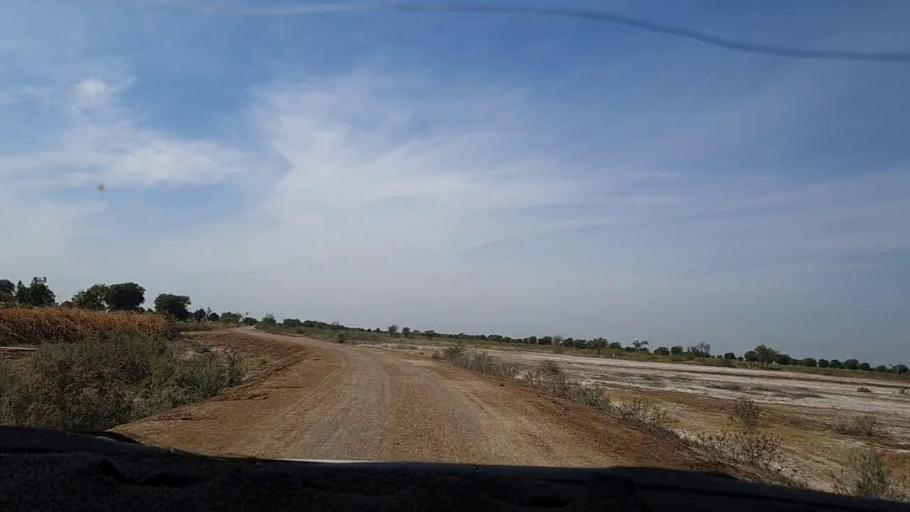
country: PK
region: Sindh
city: Dhoro Naro
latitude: 25.5024
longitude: 69.4765
